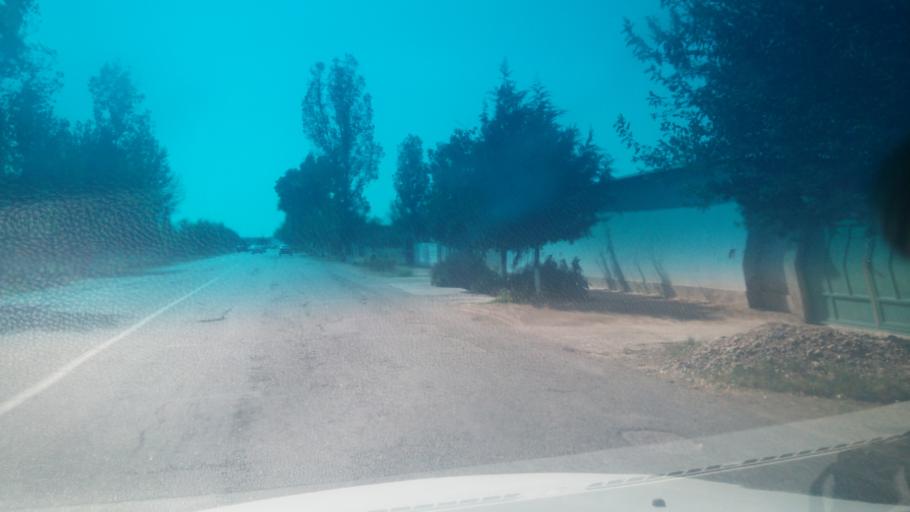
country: UZ
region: Sirdaryo
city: Sirdaryo
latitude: 40.8101
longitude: 68.6757
